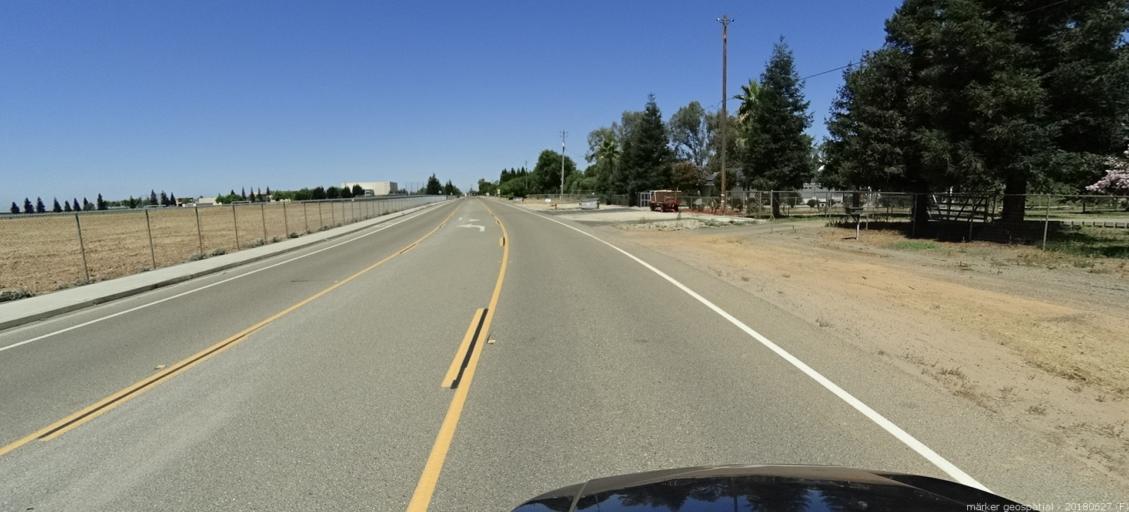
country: US
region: California
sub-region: Madera County
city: Bonadelle Ranchos-Madera Ranchos
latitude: 36.9302
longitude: -119.8972
